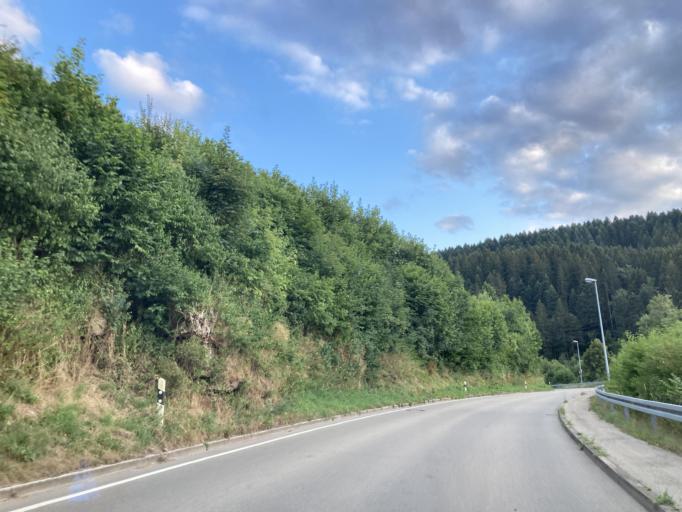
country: DE
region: Baden-Wuerttemberg
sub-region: Karlsruhe Region
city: Glatten
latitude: 48.4186
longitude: 8.5274
